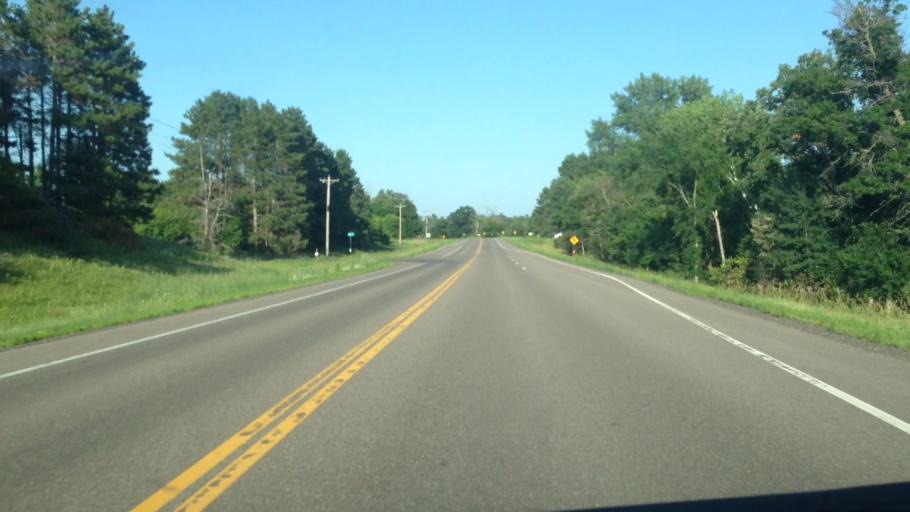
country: US
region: Minnesota
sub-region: Sherburne County
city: Zimmerman
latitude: 45.4438
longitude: -93.6482
